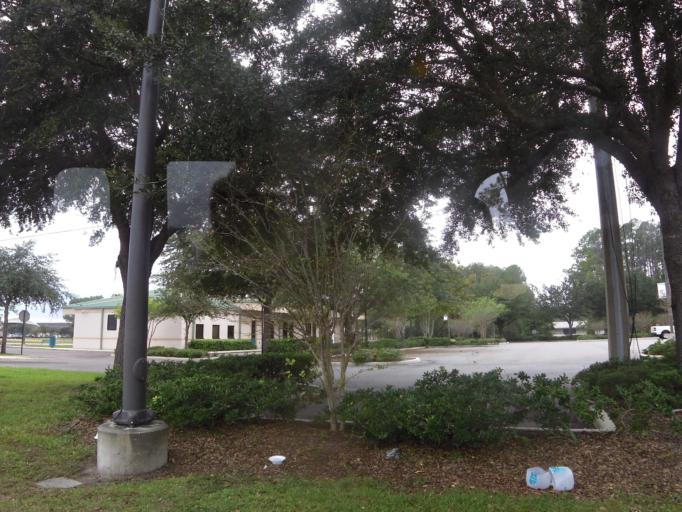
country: US
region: Florida
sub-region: Duval County
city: Baldwin
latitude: 30.2248
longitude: -81.8863
